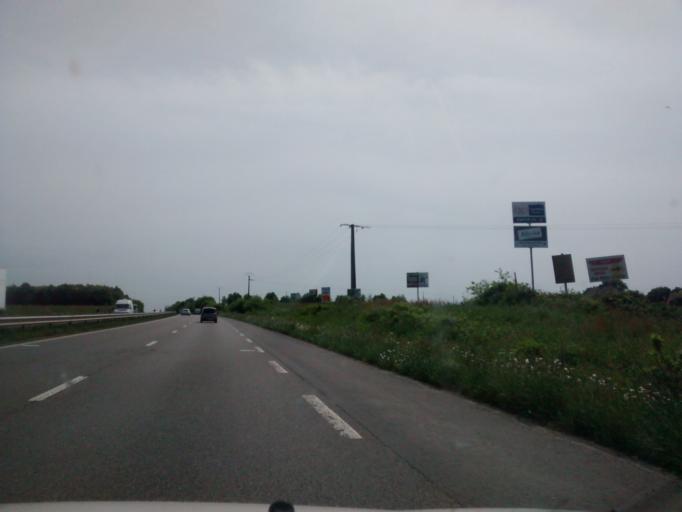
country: FR
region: Brittany
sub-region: Departement d'Ille-et-Vilaine
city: La Meziere
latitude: 48.2310
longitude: -1.7556
